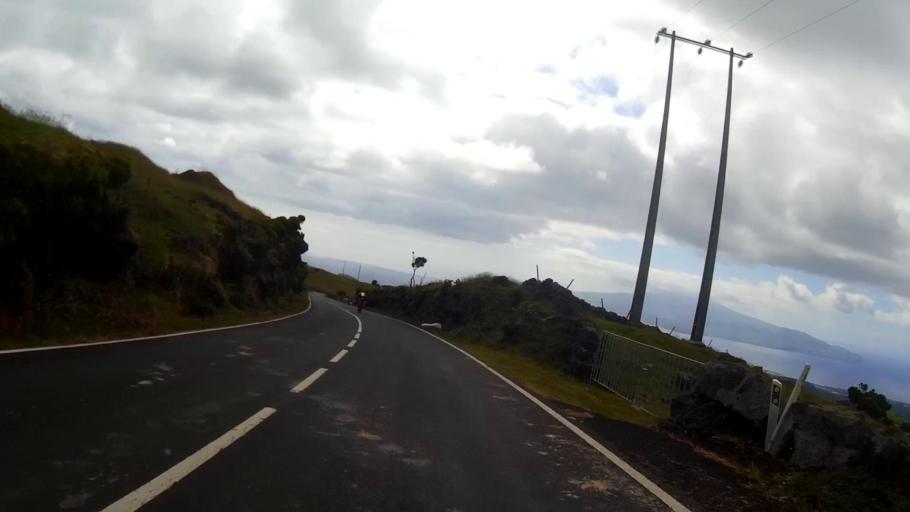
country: PT
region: Azores
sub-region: Madalena
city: Madalena
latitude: 38.4966
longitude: -28.4439
